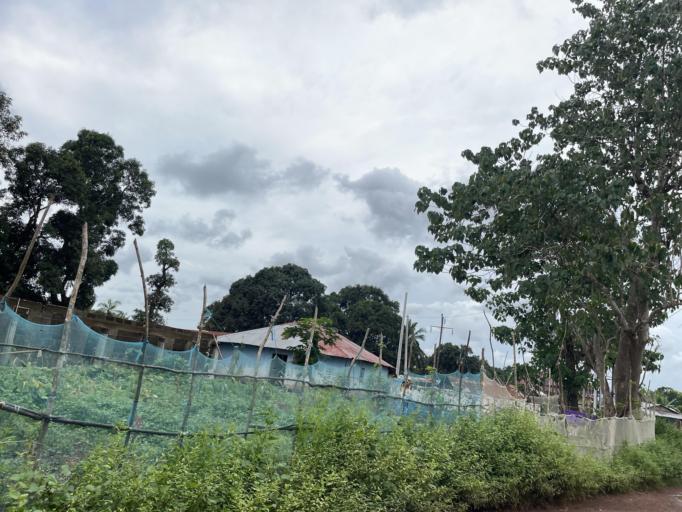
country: SL
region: Northern Province
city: Kambia
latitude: 9.1275
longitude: -12.9079
